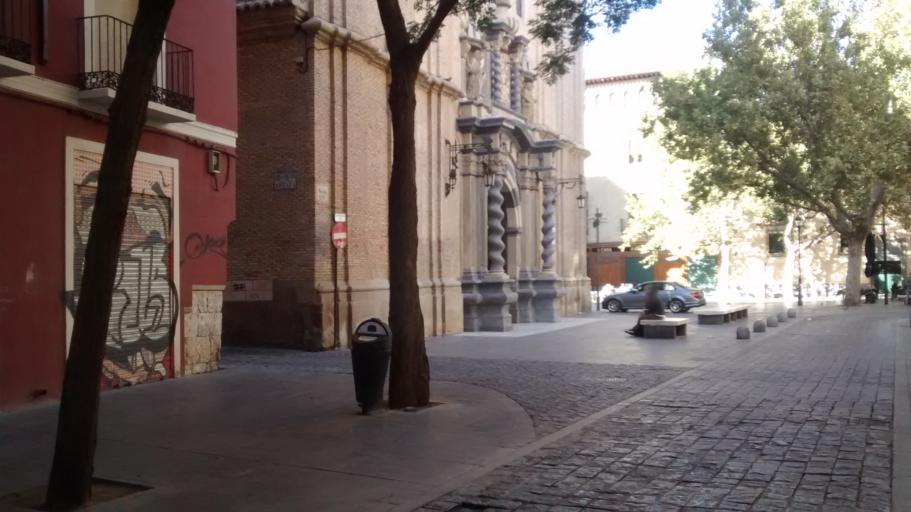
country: ES
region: Aragon
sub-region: Provincia de Zaragoza
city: Zaragoza
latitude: 41.6542
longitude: -0.8823
